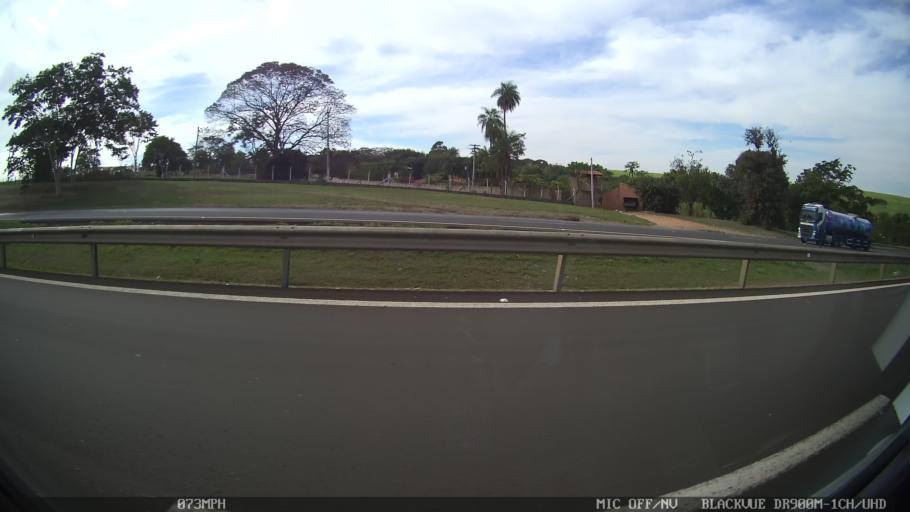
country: BR
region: Sao Paulo
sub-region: Matao
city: Matao
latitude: -21.5782
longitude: -48.4545
